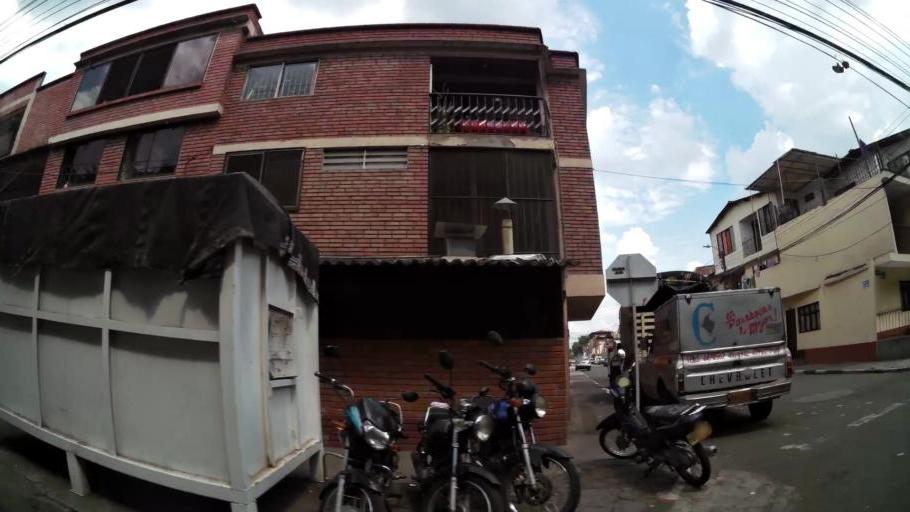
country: CO
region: Valle del Cauca
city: Cali
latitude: 3.4874
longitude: -76.5033
